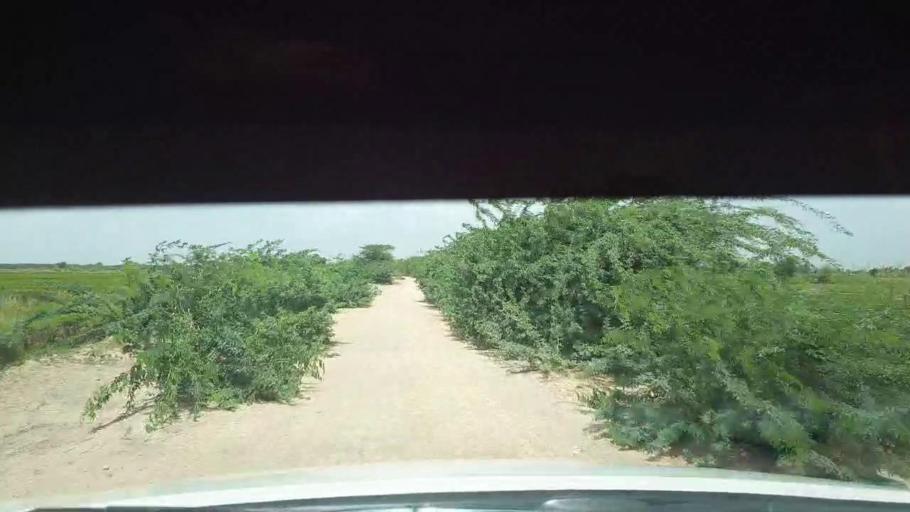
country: PK
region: Sindh
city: Kadhan
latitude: 24.5470
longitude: 68.9727
